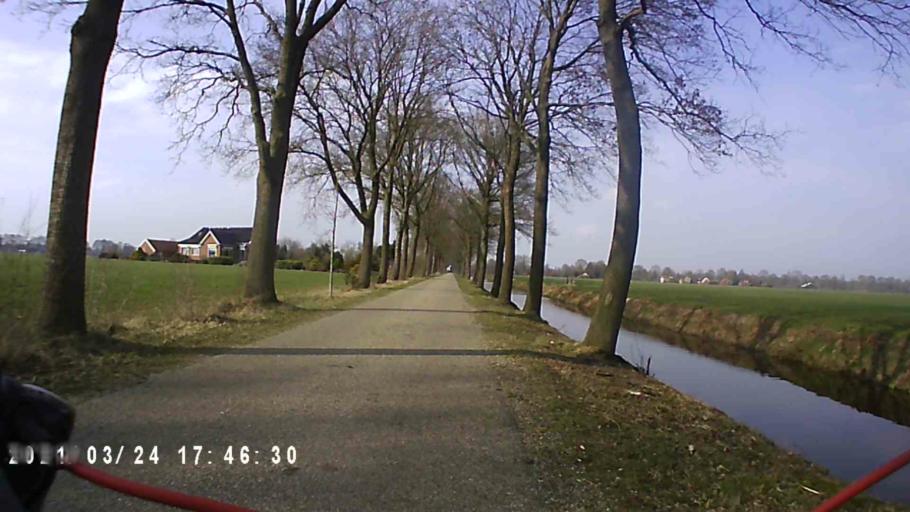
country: NL
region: Groningen
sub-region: Gemeente Leek
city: Leek
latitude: 53.1115
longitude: 6.3366
